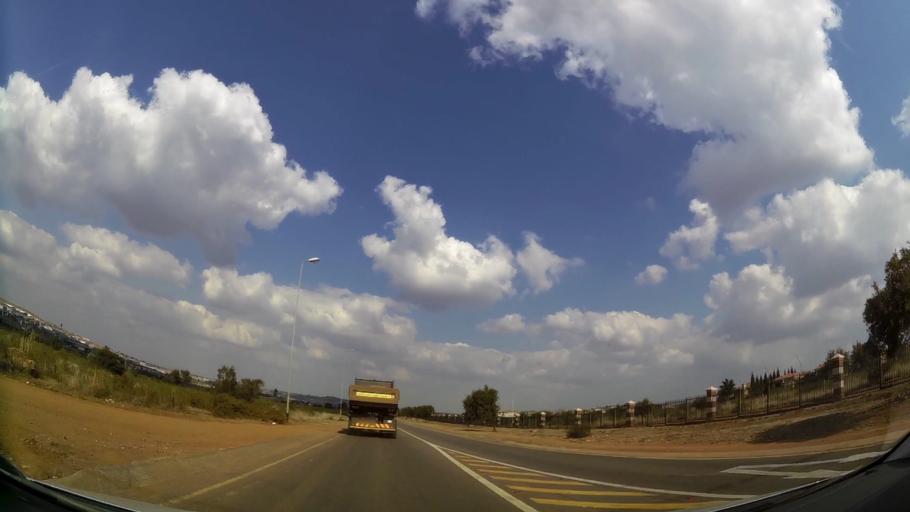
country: ZA
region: Gauteng
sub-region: City of Tshwane Metropolitan Municipality
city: Centurion
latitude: -25.8540
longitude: 28.2470
